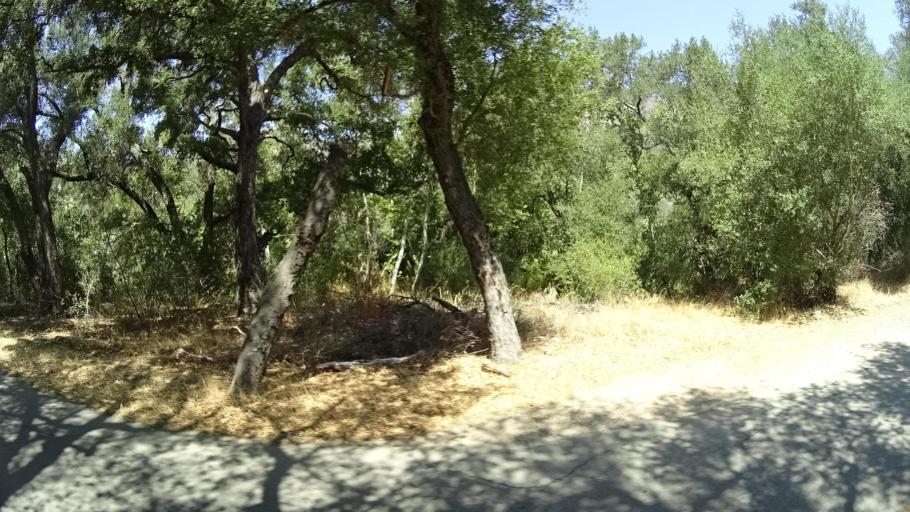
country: US
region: California
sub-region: San Diego County
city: Fallbrook
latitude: 33.4575
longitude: -117.2947
